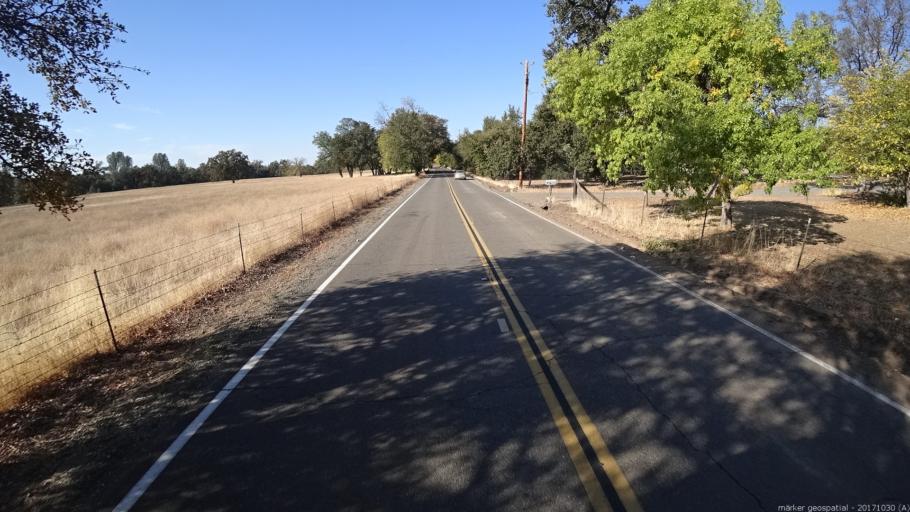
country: US
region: California
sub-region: Shasta County
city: Palo Cedro
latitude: 40.5665
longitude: -122.2083
